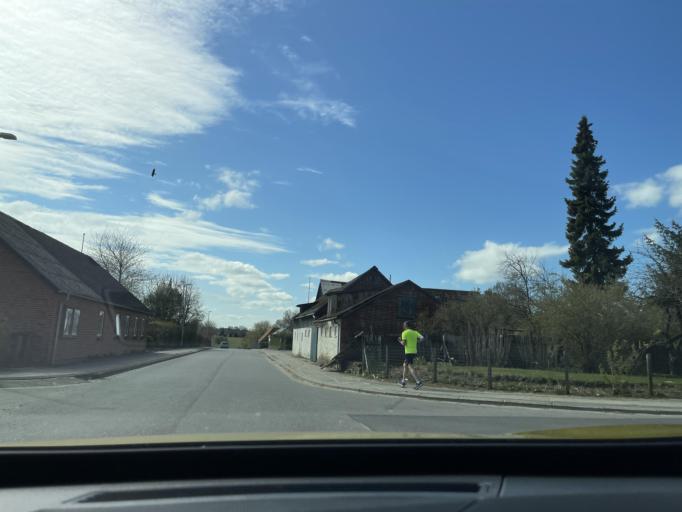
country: DK
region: Central Jutland
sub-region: Favrskov Kommune
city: Hadsten
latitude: 56.3102
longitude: 10.0952
